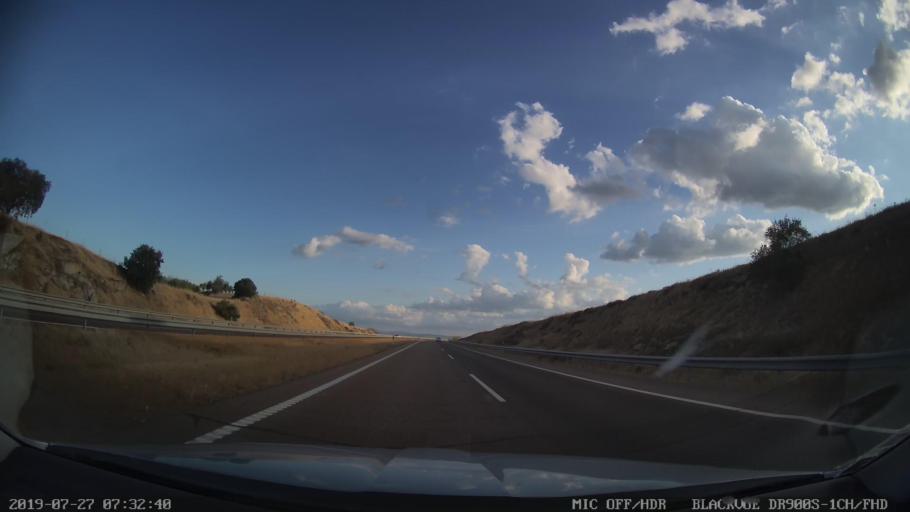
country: ES
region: Extremadura
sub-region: Provincia de Caceres
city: Miajadas
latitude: 39.1554
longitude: -5.9256
